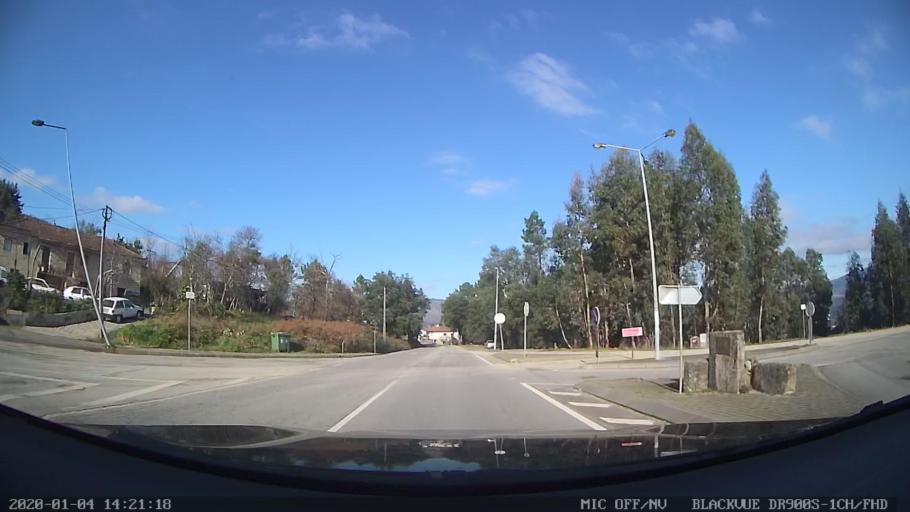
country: PT
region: Braga
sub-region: Celorico de Basto
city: Celorico de Basto
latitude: 41.4045
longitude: -7.9886
